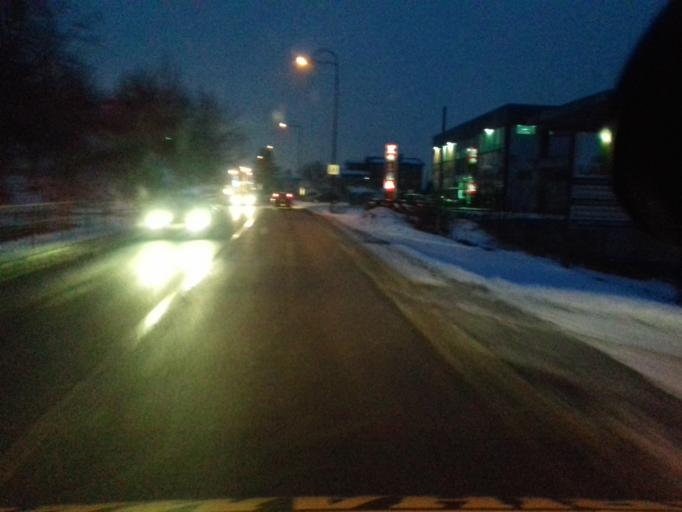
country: BA
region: Federation of Bosnia and Herzegovina
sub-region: Kanton Sarajevo
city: Sarajevo
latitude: 43.8592
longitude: 18.3201
